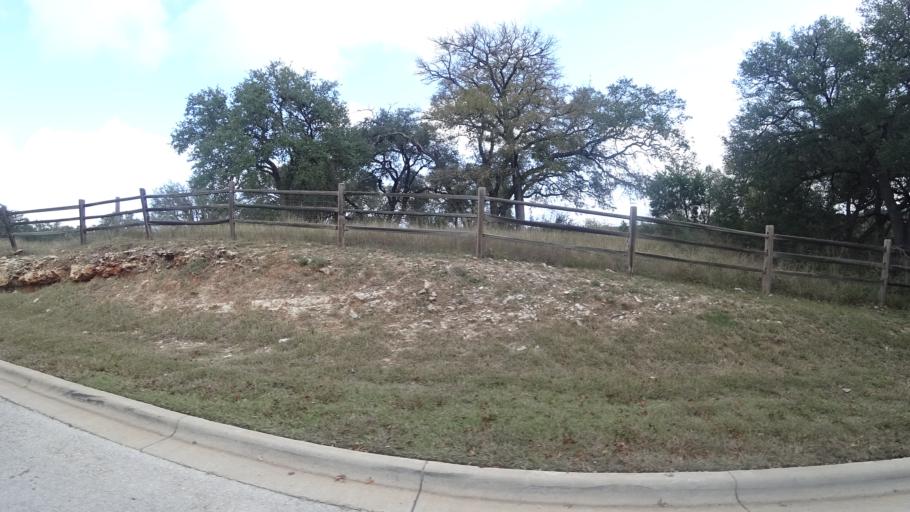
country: US
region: Texas
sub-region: Travis County
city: Bee Cave
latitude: 30.2957
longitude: -97.9289
